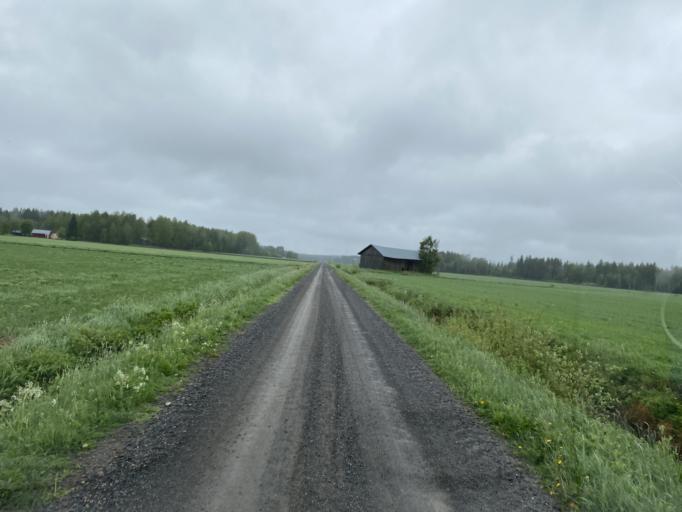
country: FI
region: Pirkanmaa
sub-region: Etelae-Pirkanmaa
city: Urjala
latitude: 60.9619
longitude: 23.5909
